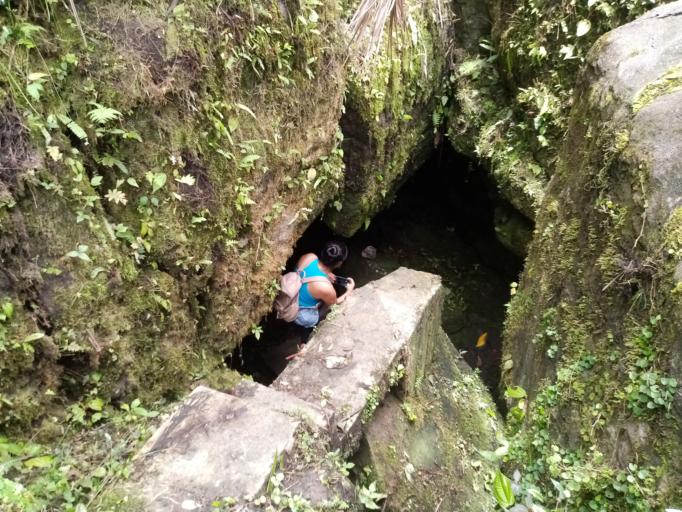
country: EC
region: Napo
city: Tena
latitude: -0.9692
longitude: -77.7974
